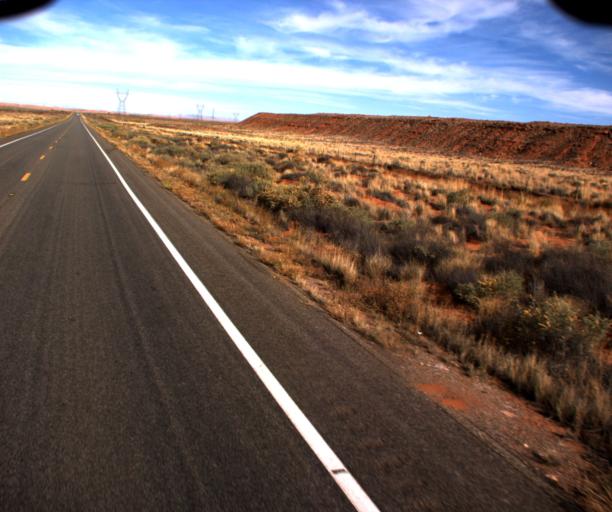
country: US
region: Arizona
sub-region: Navajo County
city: Kayenta
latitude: 36.7986
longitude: -109.9298
